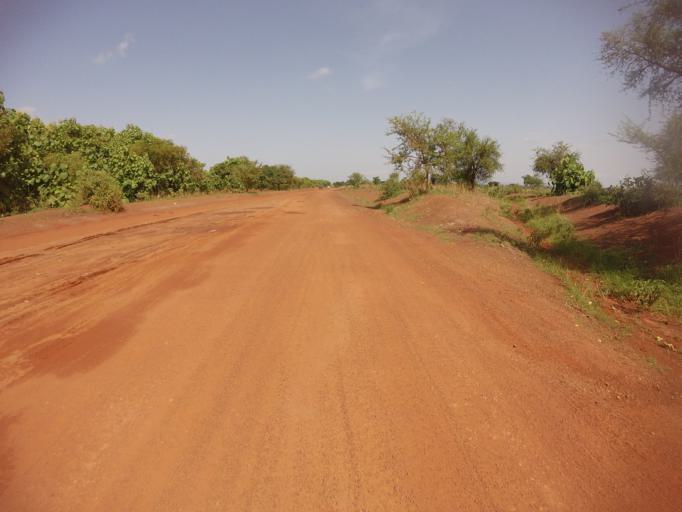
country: GH
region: Upper East
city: Bawku
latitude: 11.0002
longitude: -0.1951
